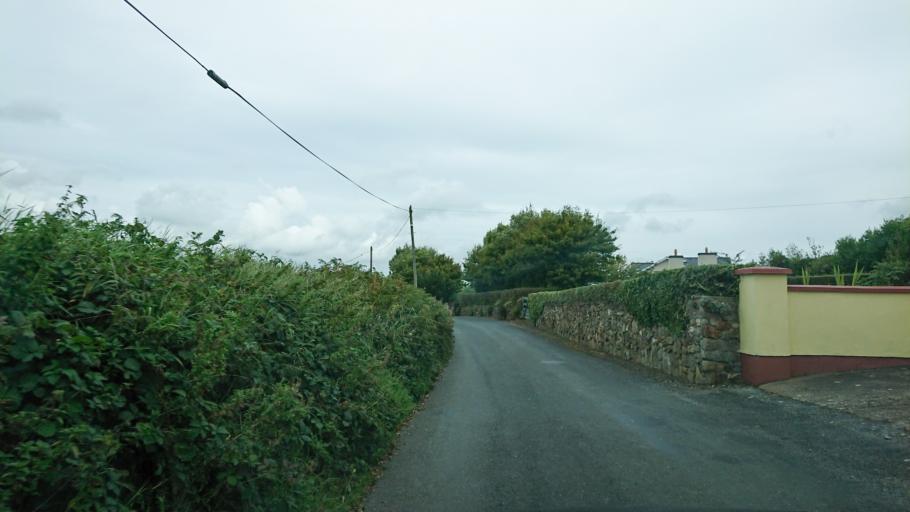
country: IE
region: Munster
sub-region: Waterford
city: Waterford
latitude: 52.2165
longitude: -7.0411
